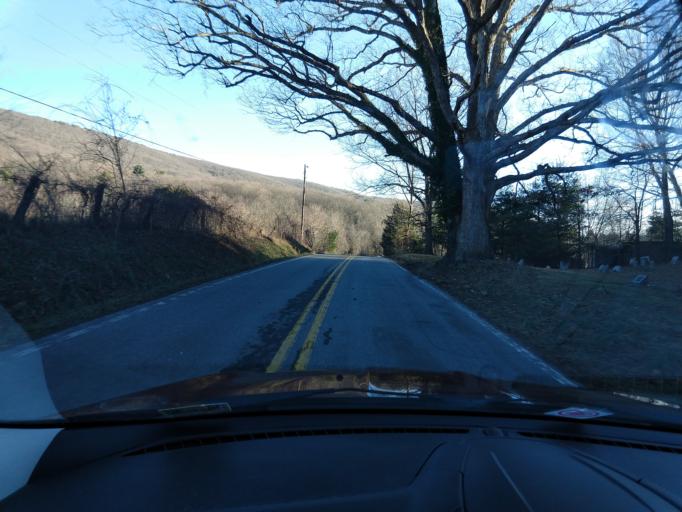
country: US
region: Virginia
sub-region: Alleghany County
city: Clifton Forge
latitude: 37.8988
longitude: -79.8904
